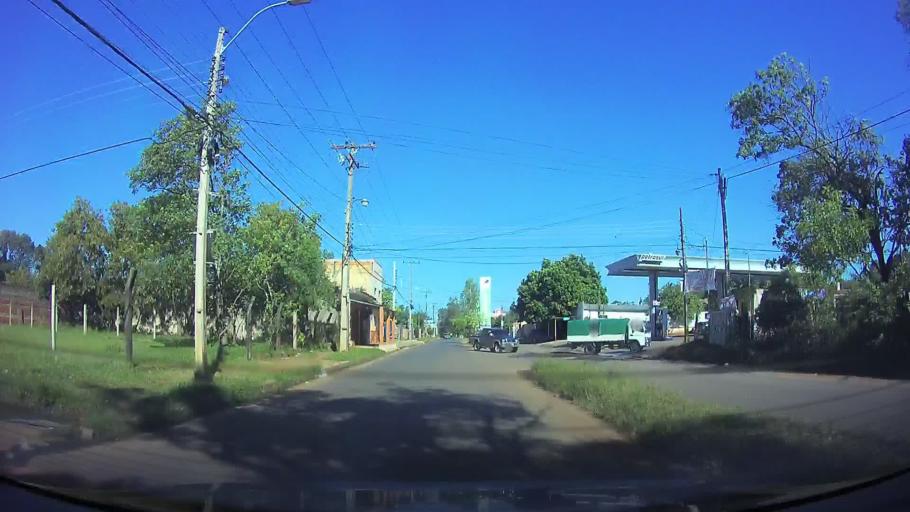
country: PY
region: Central
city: Fernando de la Mora
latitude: -25.2963
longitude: -57.5197
